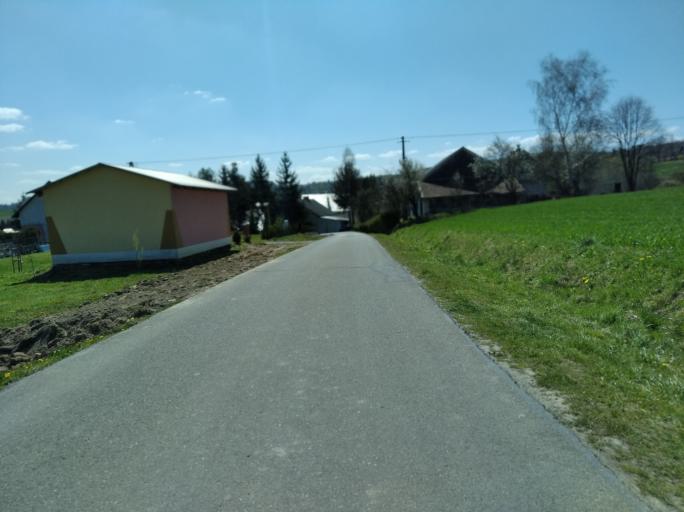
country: PL
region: Subcarpathian Voivodeship
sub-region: Powiat strzyzowski
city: Wisniowa
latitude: 49.9113
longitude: 21.6772
